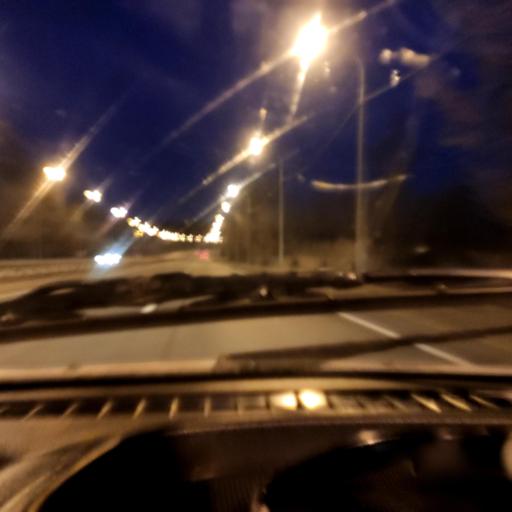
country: RU
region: Samara
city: Zhigulevsk
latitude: 53.5292
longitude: 49.5213
